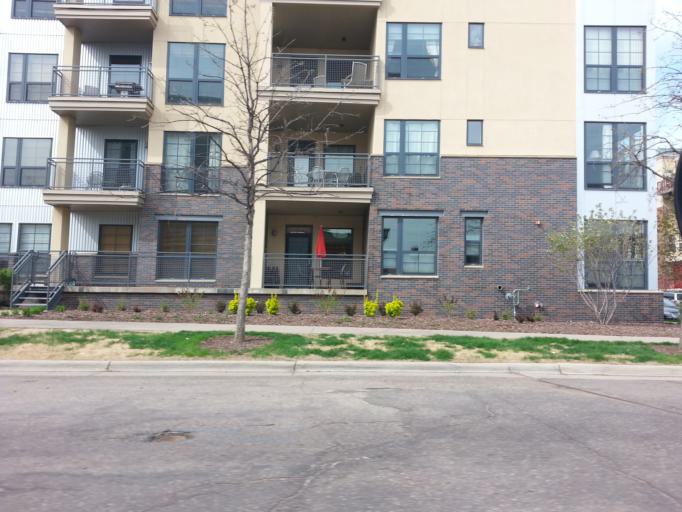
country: US
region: Minnesota
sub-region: Ramsey County
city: Lauderdale
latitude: 44.9647
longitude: -93.2068
